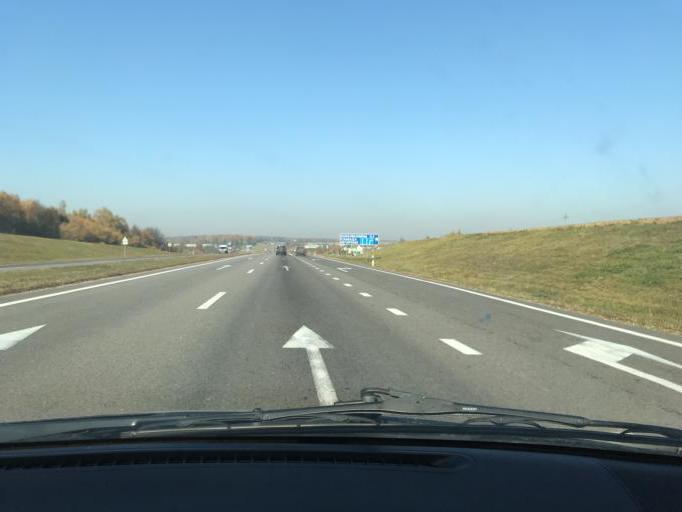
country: BY
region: Minsk
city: Samakhvalavichy
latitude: 53.7349
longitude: 27.5166
